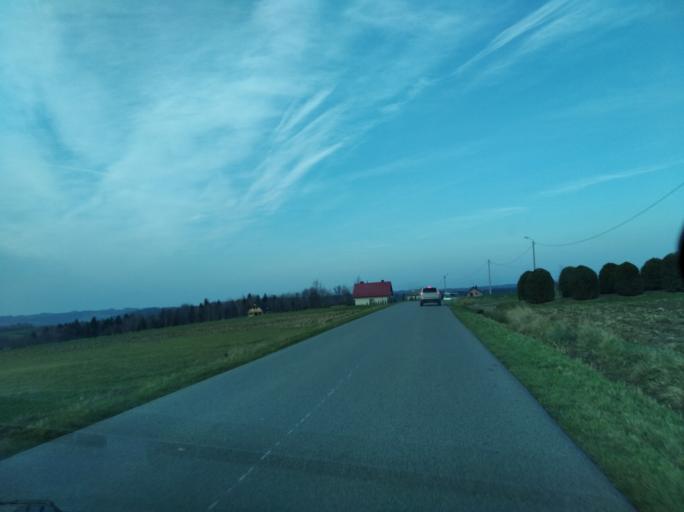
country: PL
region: Subcarpathian Voivodeship
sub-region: Powiat ropczycko-sedziszowski
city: Zagorzyce
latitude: 49.9825
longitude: 21.7137
